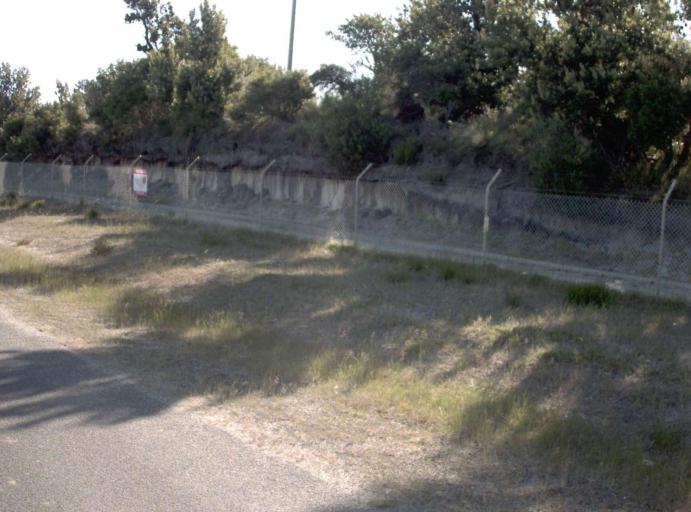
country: AU
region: Victoria
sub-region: Latrobe
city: Morwell
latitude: -38.7138
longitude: 146.3960
